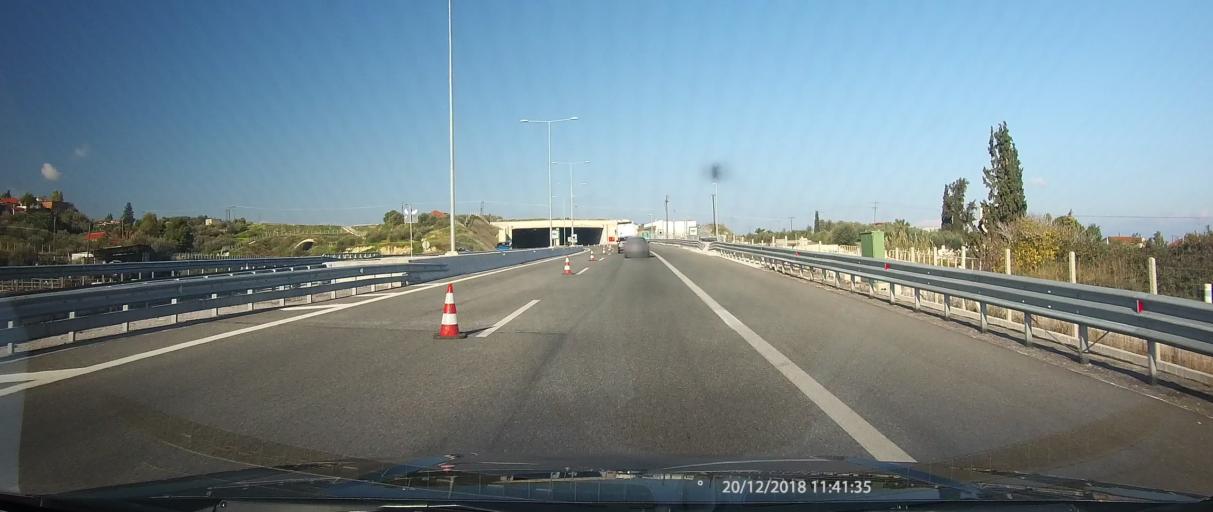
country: GR
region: Peloponnese
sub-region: Nomos Korinthias
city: Xylokastro
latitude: 38.0612
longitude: 22.6565
